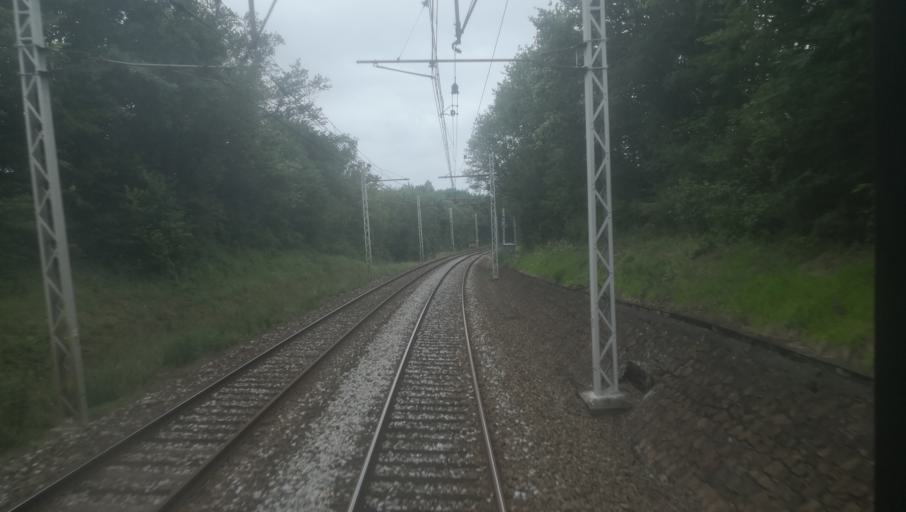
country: FR
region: Centre
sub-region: Departement de l'Indre
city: Le Pechereau
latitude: 46.5558
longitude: 1.5316
